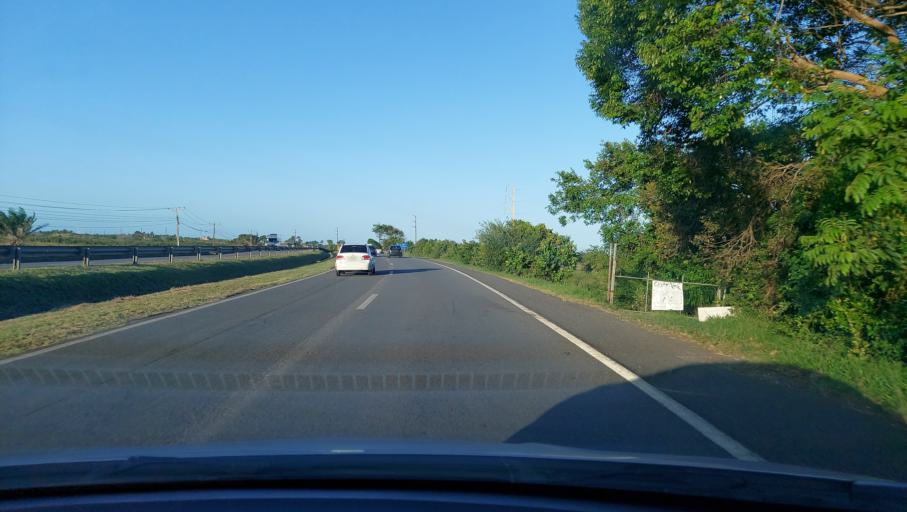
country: BR
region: Bahia
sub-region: Camacari
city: Camacari
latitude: -12.7512
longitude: -38.1693
